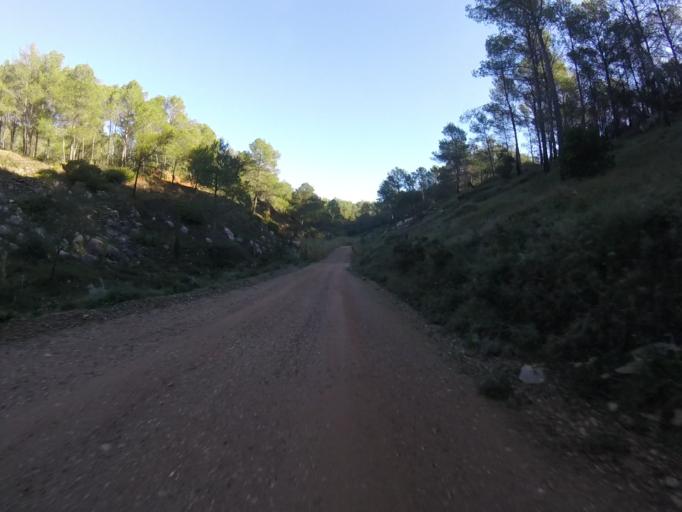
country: ES
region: Valencia
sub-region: Provincia de Castello
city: Alcala de Xivert
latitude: 40.3092
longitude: 0.2764
